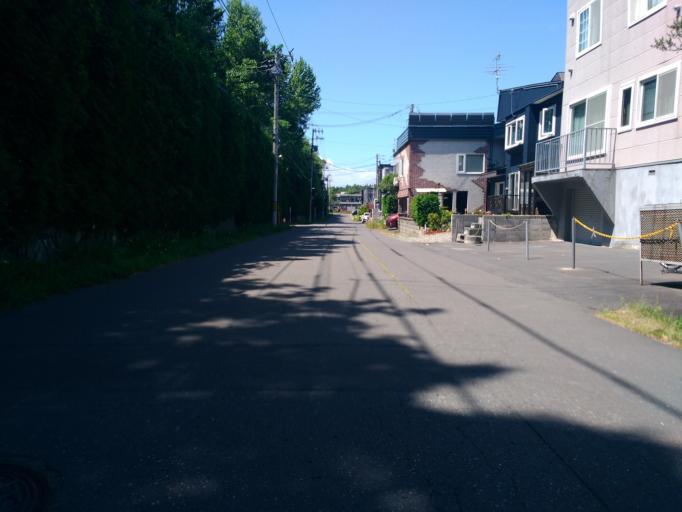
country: JP
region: Hokkaido
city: Ebetsu
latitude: 43.0678
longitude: 141.4943
